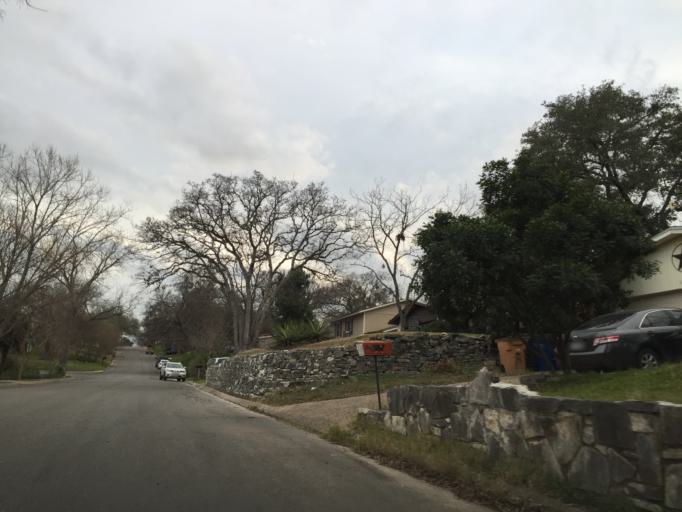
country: US
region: Texas
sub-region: Travis County
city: Wells Branch
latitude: 30.3894
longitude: -97.6790
